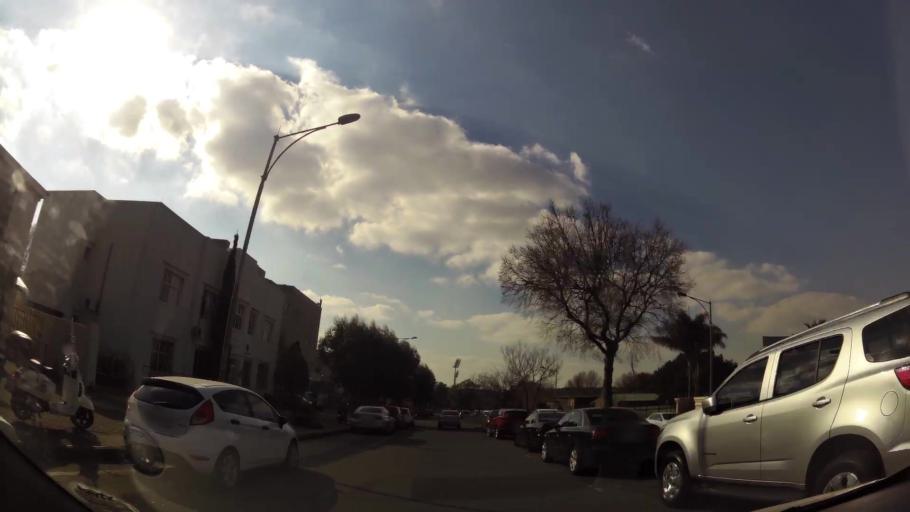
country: ZA
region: Gauteng
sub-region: West Rand District Municipality
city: Krugersdorp
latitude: -26.1057
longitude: 27.7757
